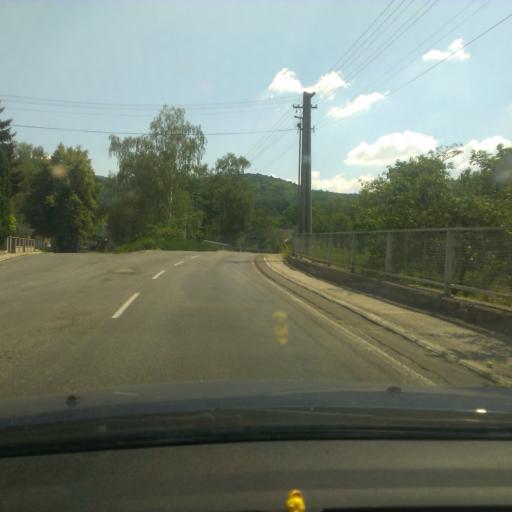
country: SK
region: Trnavsky
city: Hlohovec
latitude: 48.5083
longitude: 17.8277
